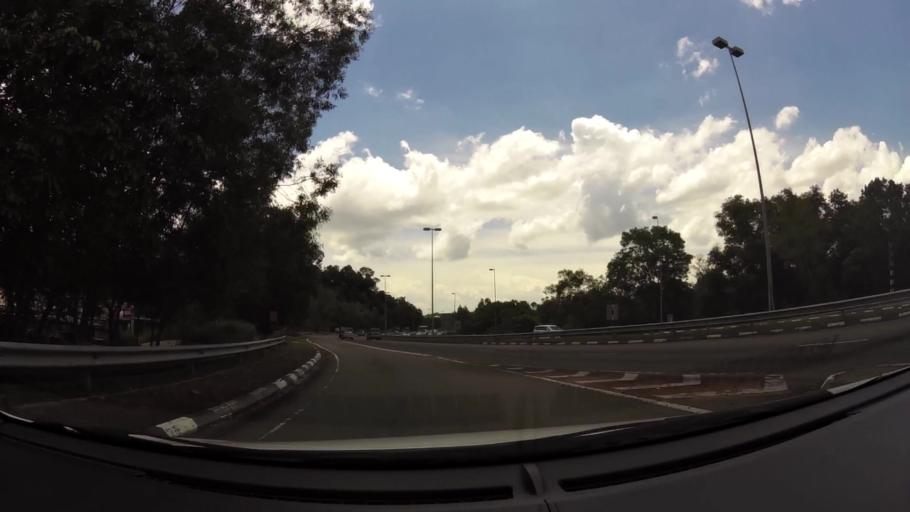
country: BN
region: Brunei and Muara
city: Bandar Seri Begawan
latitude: 4.9329
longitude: 114.9742
